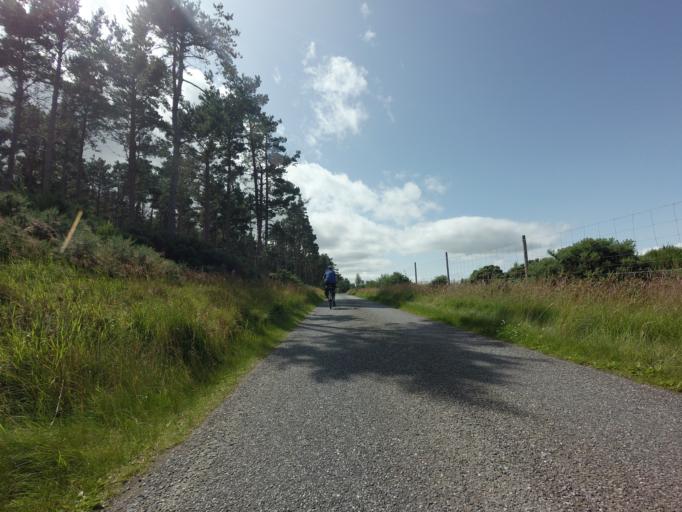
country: GB
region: Scotland
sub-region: Highland
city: Fortrose
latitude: 57.4840
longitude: -4.0327
